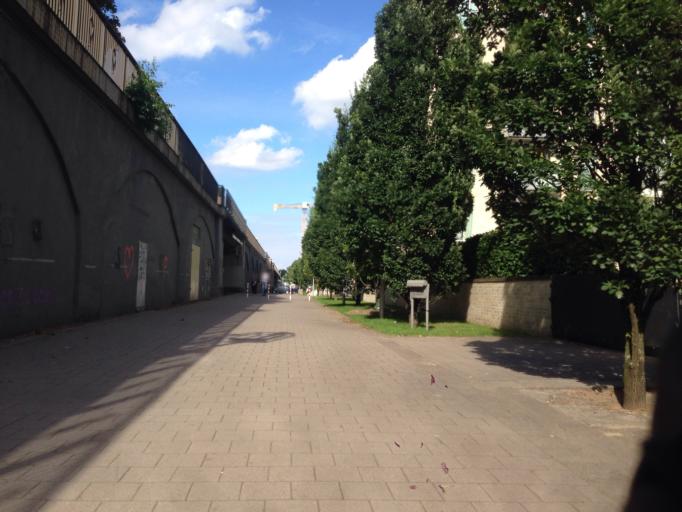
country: DE
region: Hamburg
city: Hamburg
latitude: 53.5702
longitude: 10.0291
